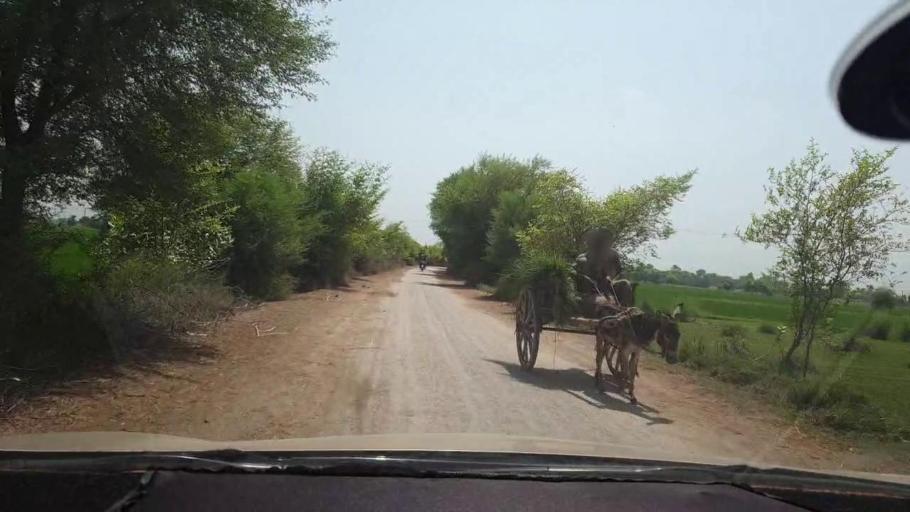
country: PK
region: Sindh
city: Kambar
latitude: 27.6624
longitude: 67.9323
